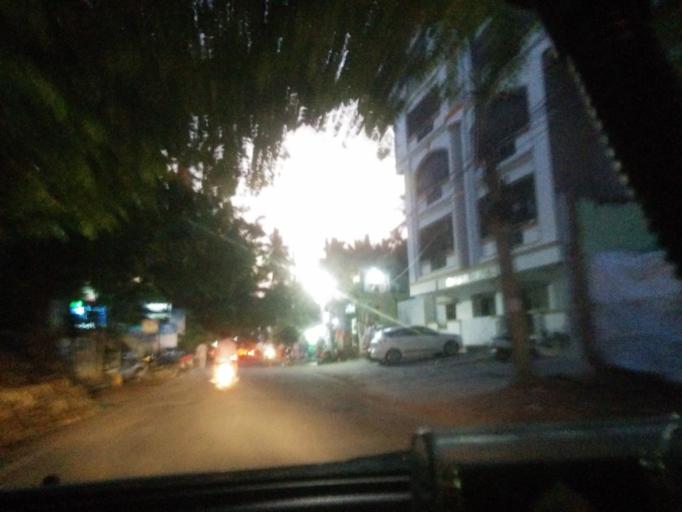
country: IN
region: Andhra Pradesh
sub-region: East Godavari
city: Rajahmundry
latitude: 17.0075
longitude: 81.7873
